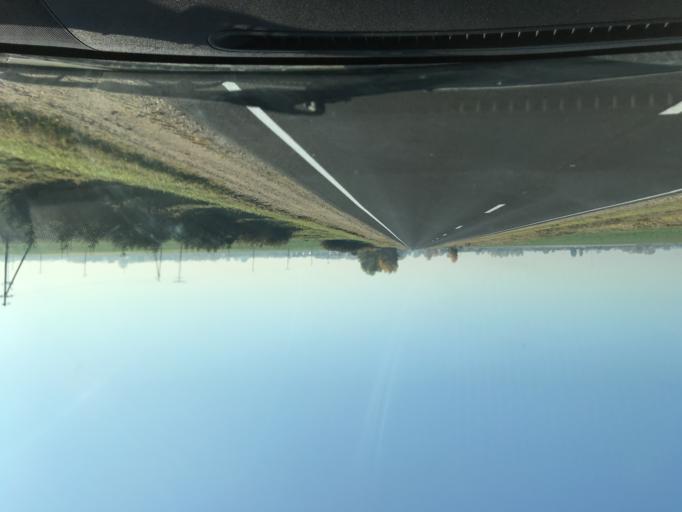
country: BY
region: Brest
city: Baranovichi
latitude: 52.8924
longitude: 25.8308
